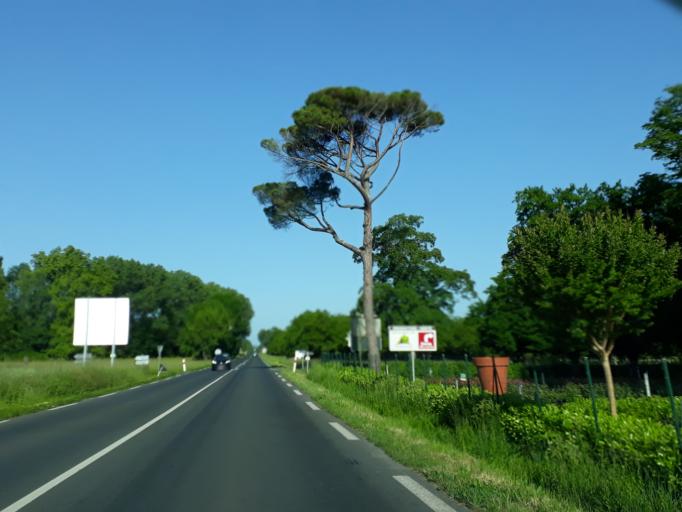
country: FR
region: Limousin
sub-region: Departement de la Correze
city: Mansac
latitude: 45.1267
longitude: 1.3663
